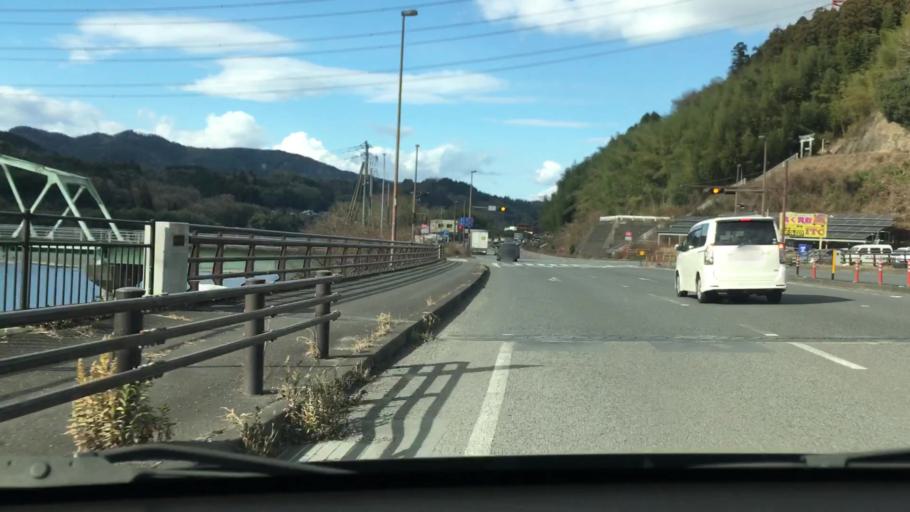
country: JP
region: Oita
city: Oita
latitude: 33.1124
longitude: 131.6562
